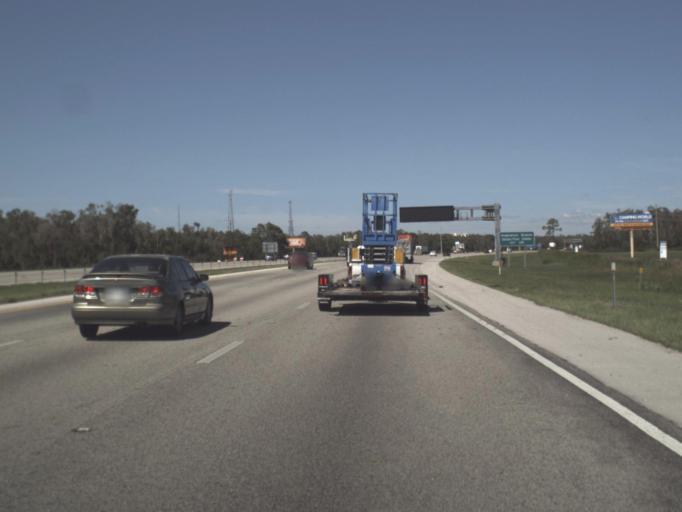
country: US
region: Florida
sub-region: Lee County
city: Fort Myers
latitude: 26.6190
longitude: -81.8048
